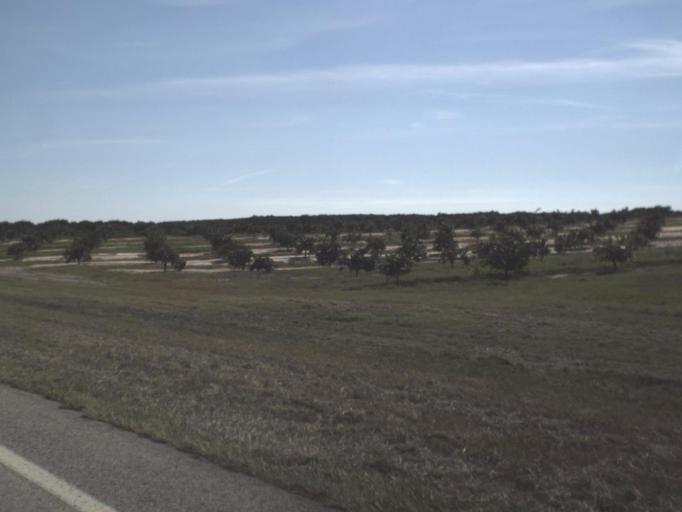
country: US
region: Florida
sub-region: Highlands County
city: Lake Placid
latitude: 27.2467
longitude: -81.3375
